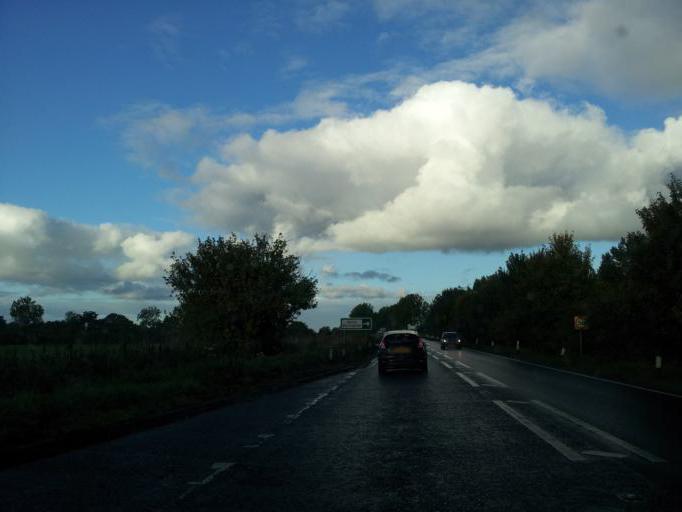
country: GB
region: England
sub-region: Norfolk
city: Lingwood
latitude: 52.6357
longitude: 1.4946
